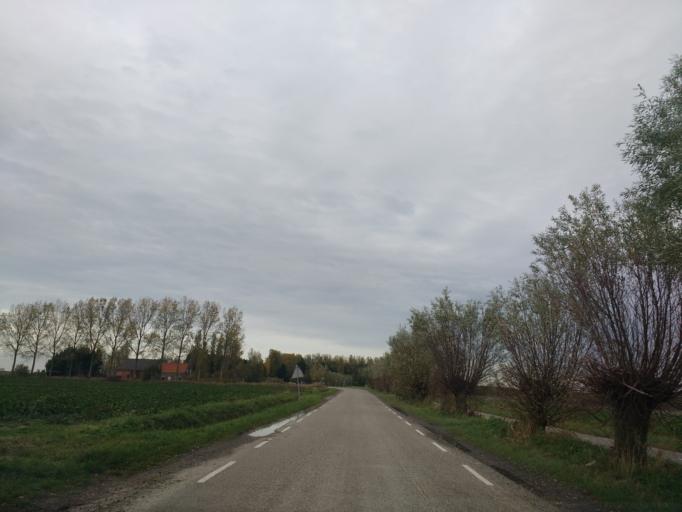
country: NL
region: Zeeland
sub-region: Gemeente Vlissingen
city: Vlissingen
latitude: 51.3849
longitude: 3.5176
